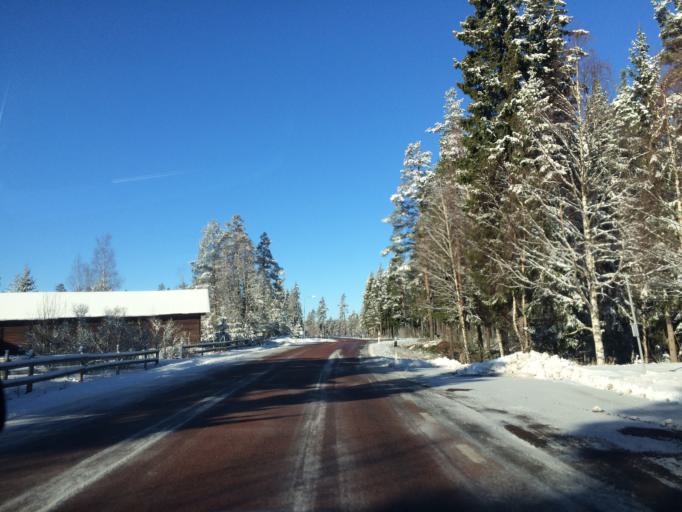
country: SE
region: Dalarna
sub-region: Mora Kommun
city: Mora
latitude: 60.8476
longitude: 14.2814
